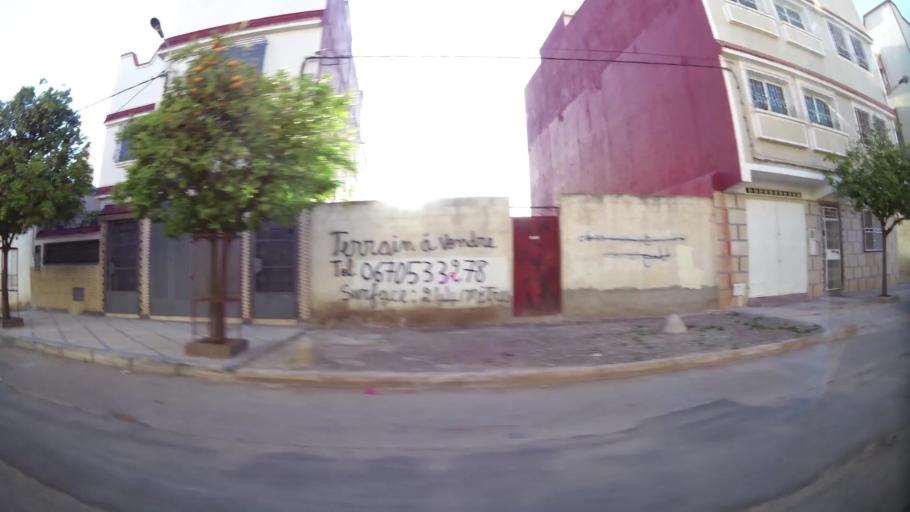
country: MA
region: Oriental
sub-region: Oujda-Angad
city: Oujda
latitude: 34.6763
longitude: -1.8970
